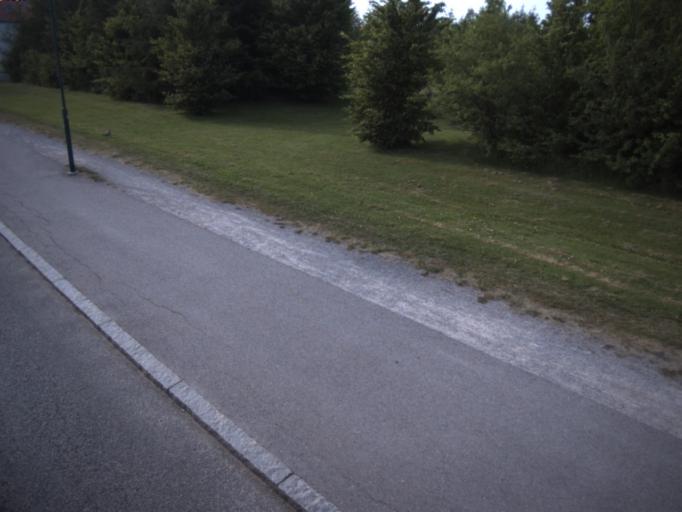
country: SE
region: Skane
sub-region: Helsingborg
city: Helsingborg
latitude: 56.0821
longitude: 12.6924
